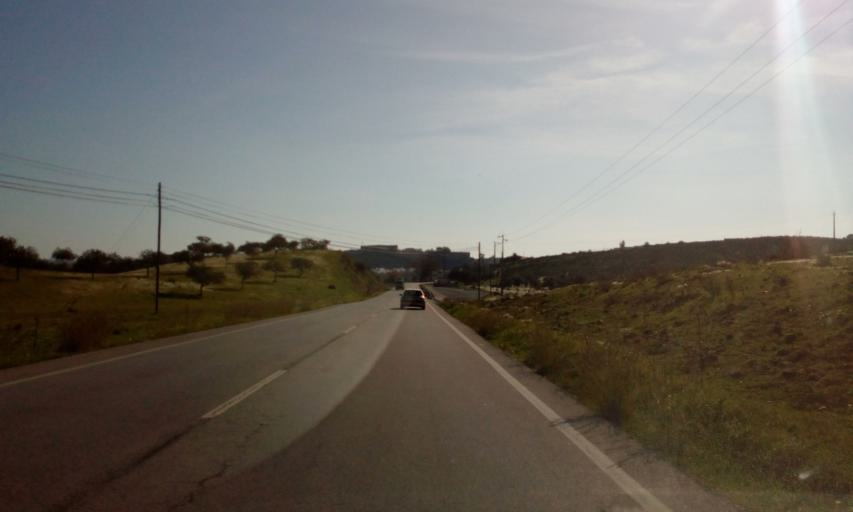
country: PT
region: Faro
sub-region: Castro Marim
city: Castro Marim
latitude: 37.2267
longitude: -7.4469
